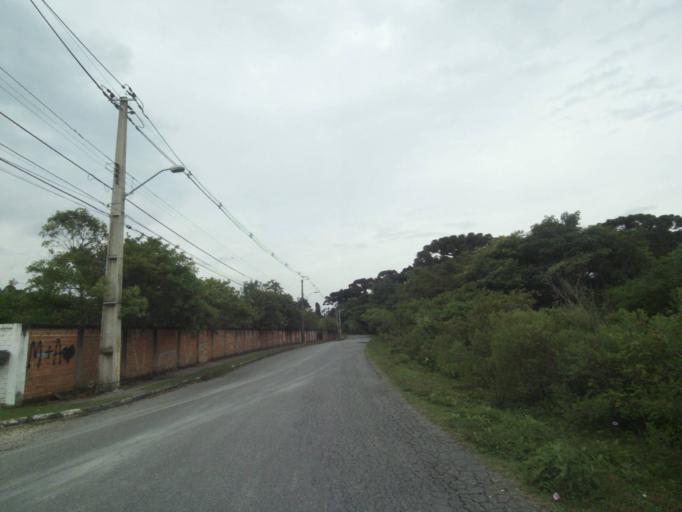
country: BR
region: Parana
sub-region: Curitiba
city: Curitiba
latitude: -25.4124
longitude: -49.3084
